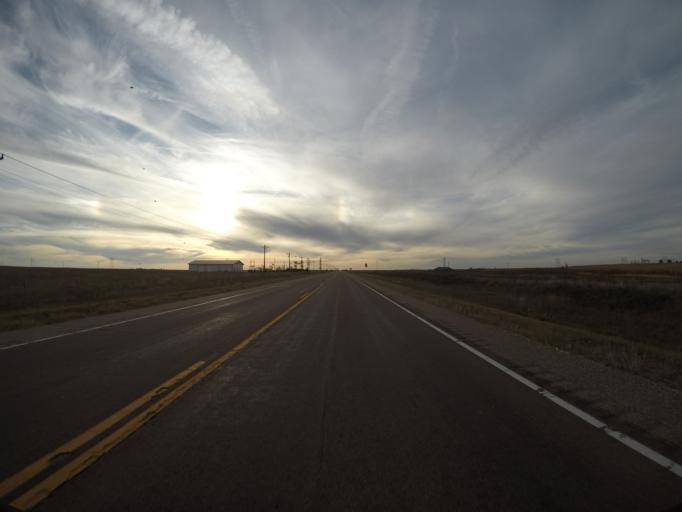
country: US
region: Colorado
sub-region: Yuma County
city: Yuma
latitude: 39.6559
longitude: -102.7037
